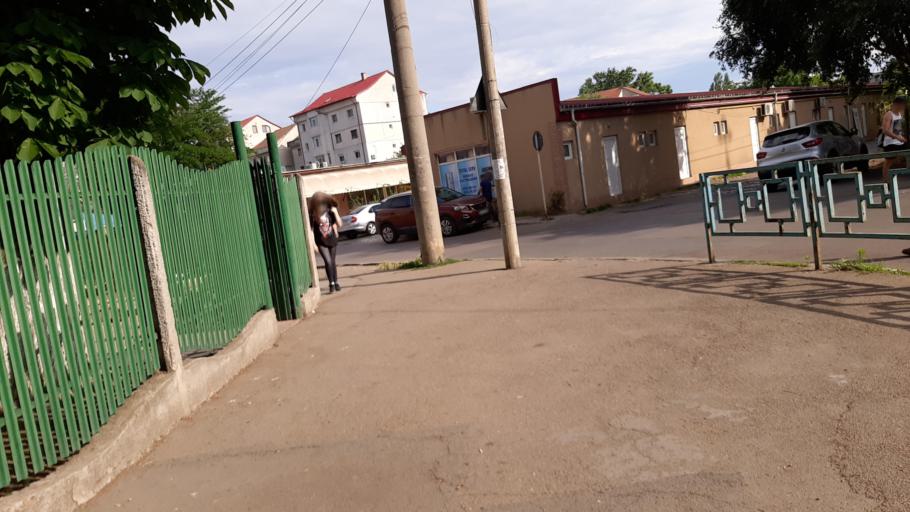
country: RO
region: Galati
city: Galati
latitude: 45.4418
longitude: 28.0263
